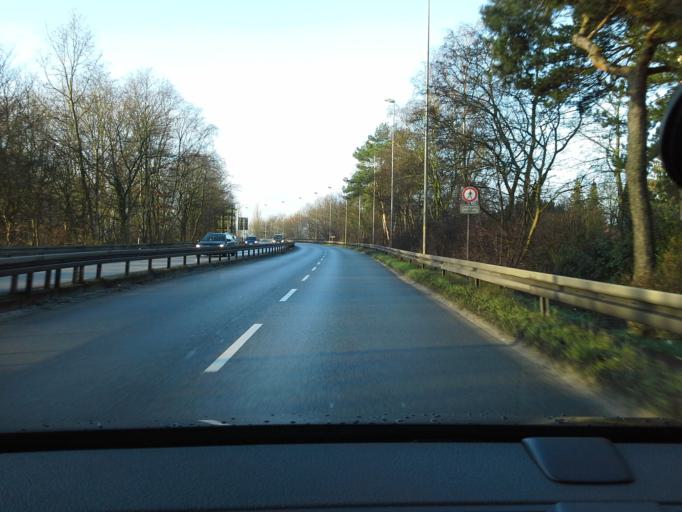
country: DE
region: Schleswig-Holstein
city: Pinneberg
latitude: 53.6634
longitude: 9.7912
